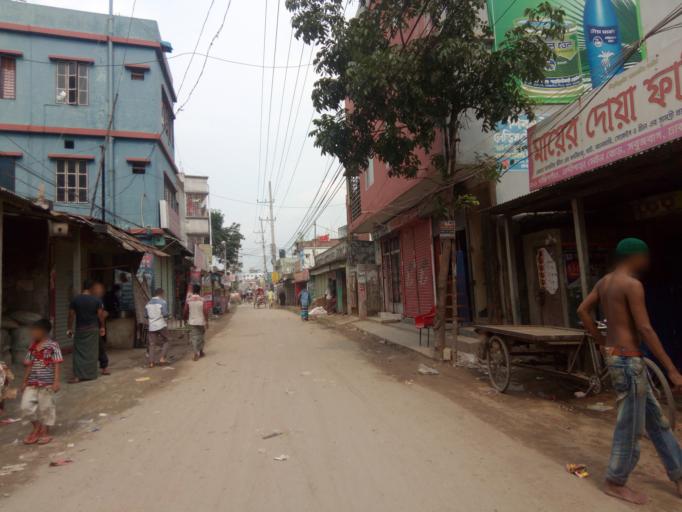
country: BD
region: Dhaka
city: Paltan
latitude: 23.7447
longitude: 90.4485
